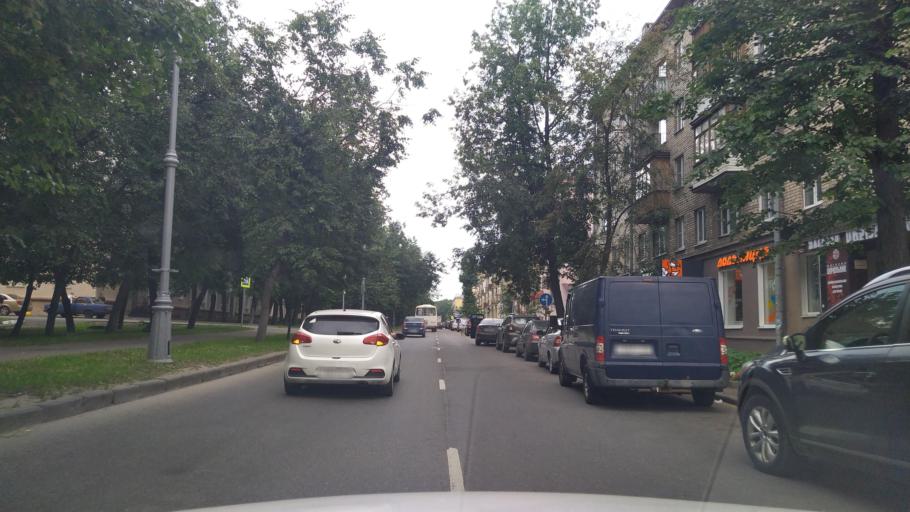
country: RU
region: Novgorod
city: Velikiy Novgorod
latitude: 58.5236
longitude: 31.2623
